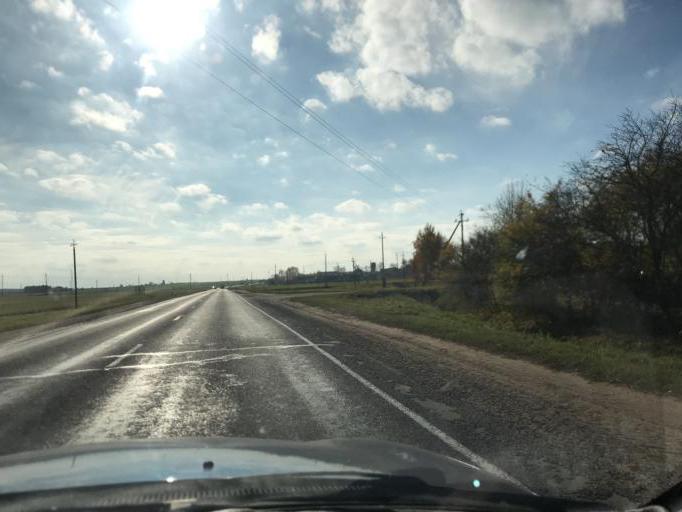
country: BY
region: Grodnenskaya
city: Voranava
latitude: 54.1527
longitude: 25.3259
